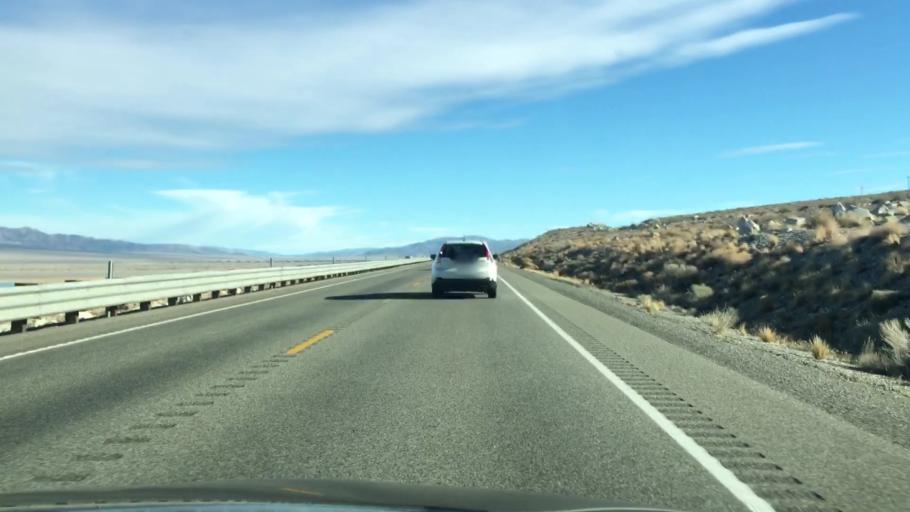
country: US
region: Nevada
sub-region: Mineral County
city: Hawthorne
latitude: 38.6151
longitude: -118.7269
